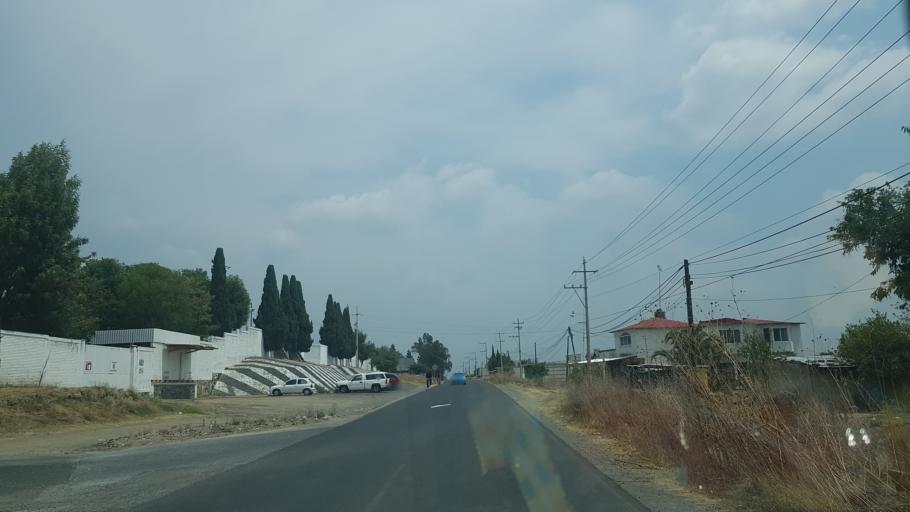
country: MX
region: Puebla
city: Huejotzingo
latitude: 19.1381
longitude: -98.4134
